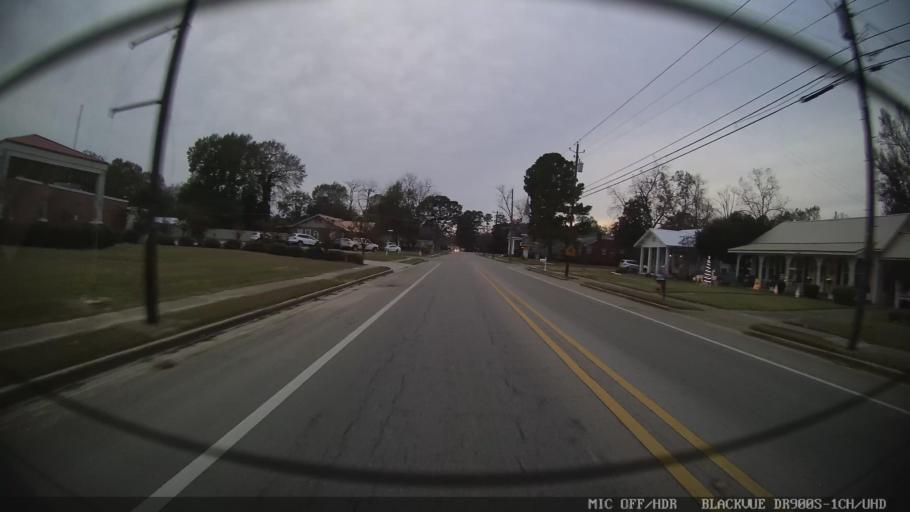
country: US
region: Mississippi
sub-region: Clarke County
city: Quitman
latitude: 32.0366
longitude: -88.7228
